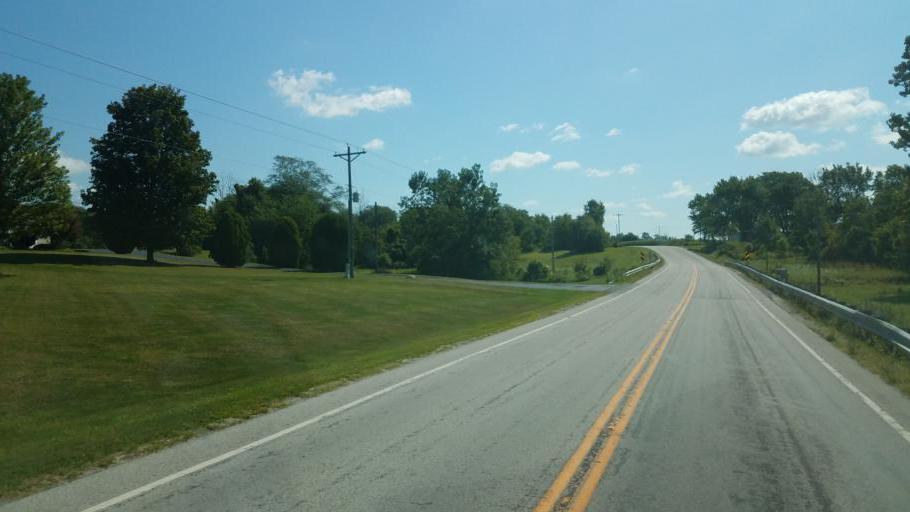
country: US
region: Ohio
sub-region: Wyandot County
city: Carey
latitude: 40.9480
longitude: -83.3450
